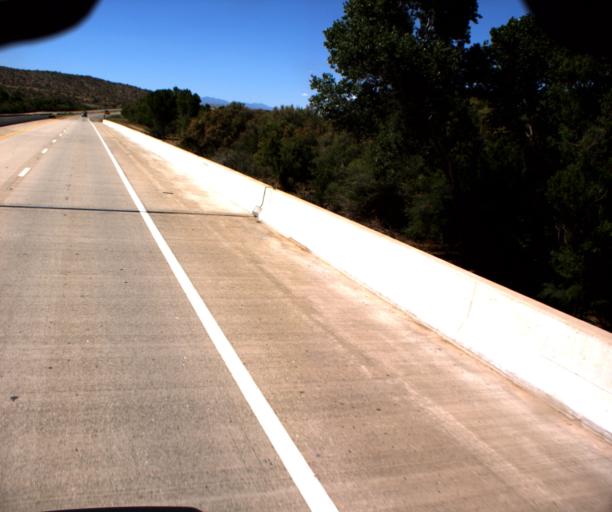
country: US
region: Arizona
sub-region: Yavapai County
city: Bagdad
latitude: 34.6635
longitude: -113.5814
